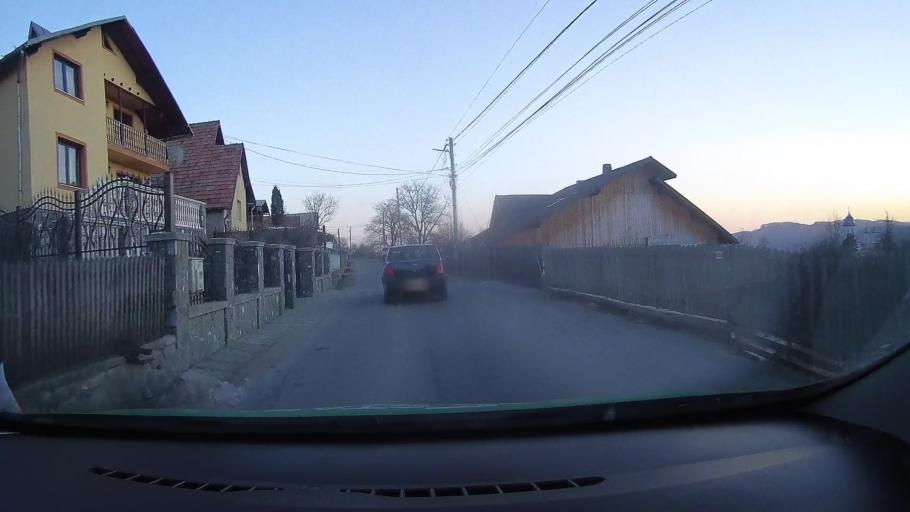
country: RO
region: Prahova
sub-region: Comuna Comarnic
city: Comarnic
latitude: 45.2481
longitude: 25.6388
